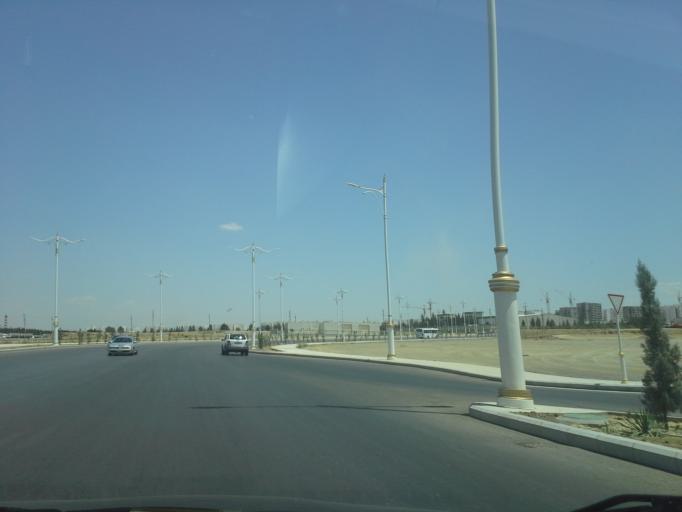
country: TM
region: Ahal
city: Ashgabat
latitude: 37.9019
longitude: 58.3978
